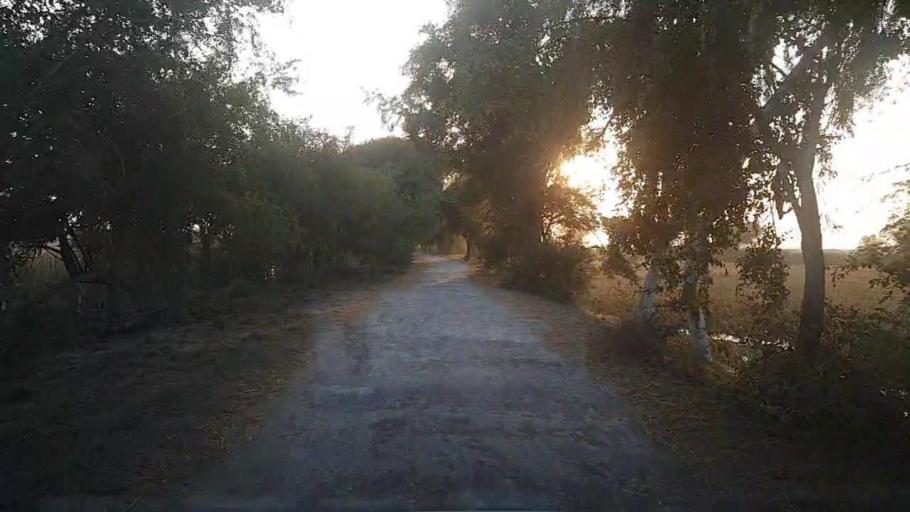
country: PK
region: Sindh
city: Mehar
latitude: 27.1835
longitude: 67.7374
